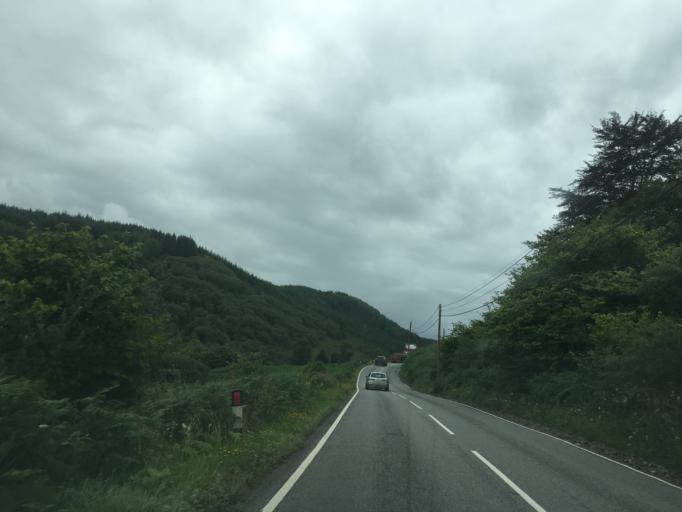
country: GB
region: Scotland
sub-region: Argyll and Bute
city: Oban
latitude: 56.2962
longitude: -5.4654
